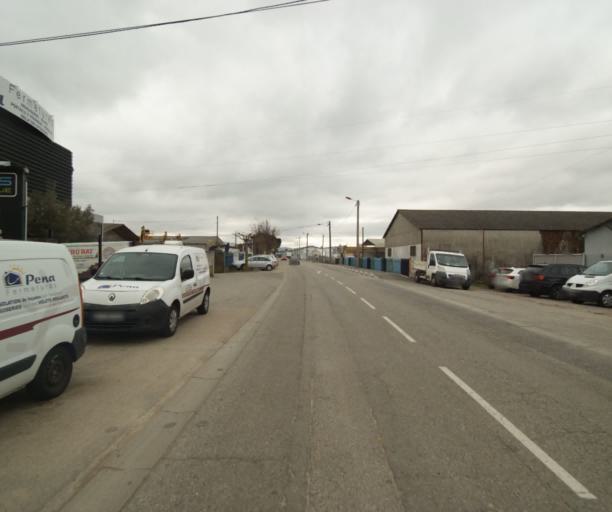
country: FR
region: Midi-Pyrenees
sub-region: Departement de l'Ariege
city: Pamiers
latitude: 43.1235
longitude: 1.6208
